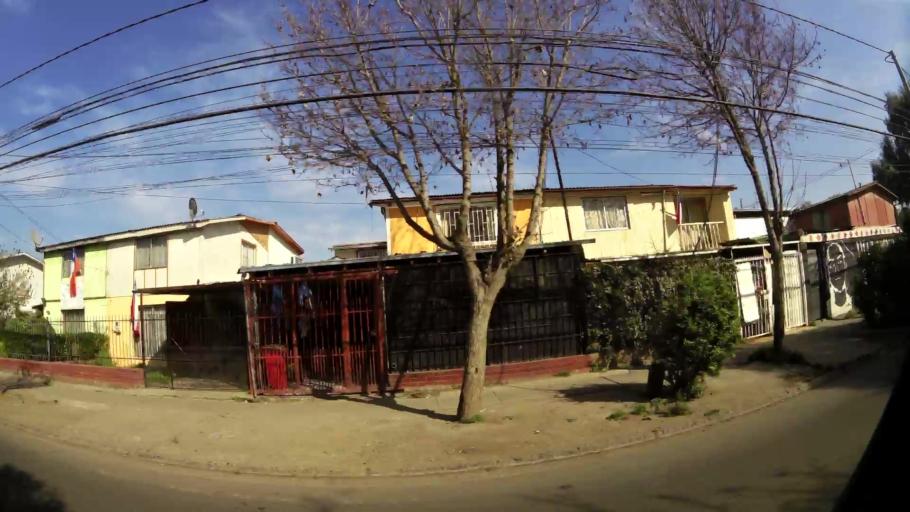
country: CL
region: Santiago Metropolitan
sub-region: Provincia de Santiago
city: Lo Prado
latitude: -33.4554
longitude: -70.7551
